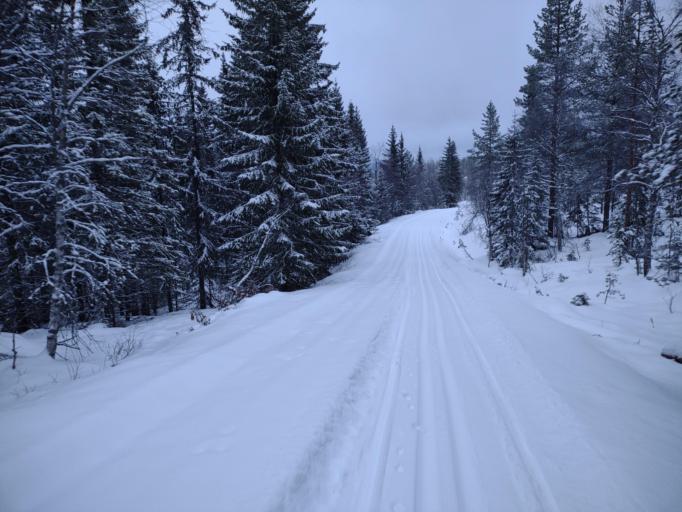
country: NO
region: Buskerud
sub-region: Flesberg
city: Lampeland
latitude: 59.7470
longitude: 9.4896
